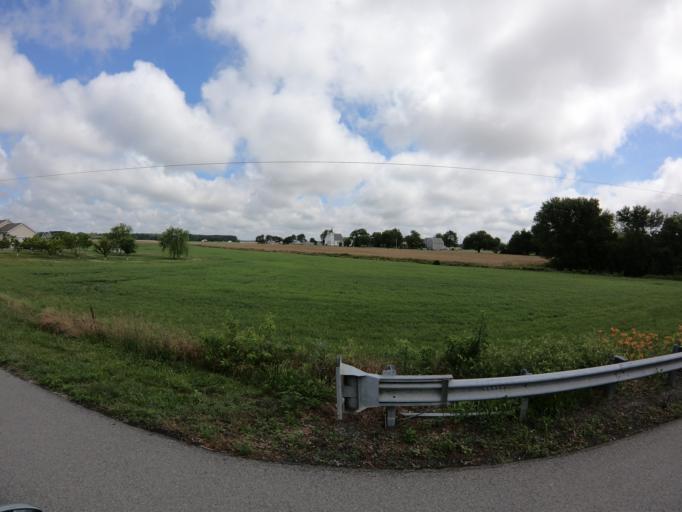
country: US
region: Maryland
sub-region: Caroline County
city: Greensboro
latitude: 39.0926
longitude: -75.8776
